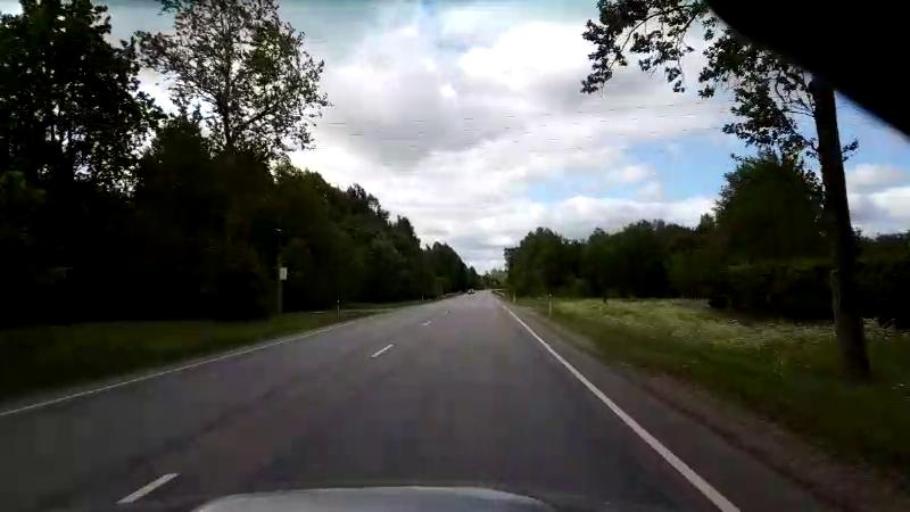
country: EE
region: Harju
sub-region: Nissi vald
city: Riisipere
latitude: 59.1042
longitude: 24.4721
